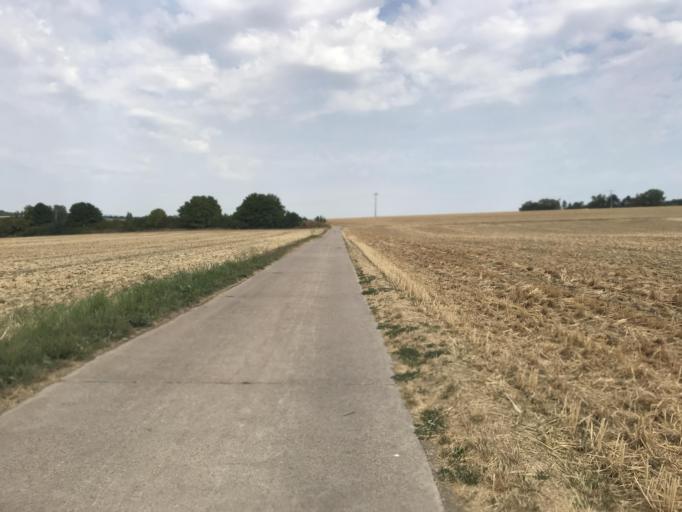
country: DE
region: Rheinland-Pfalz
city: Sorgenloch
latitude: 49.8704
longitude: 8.1984
